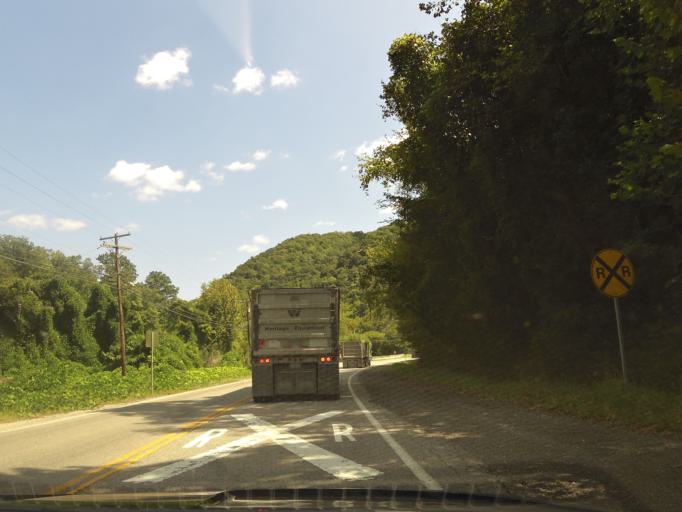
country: US
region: Kentucky
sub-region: Harlan County
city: Harlan
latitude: 36.8687
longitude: -83.3198
